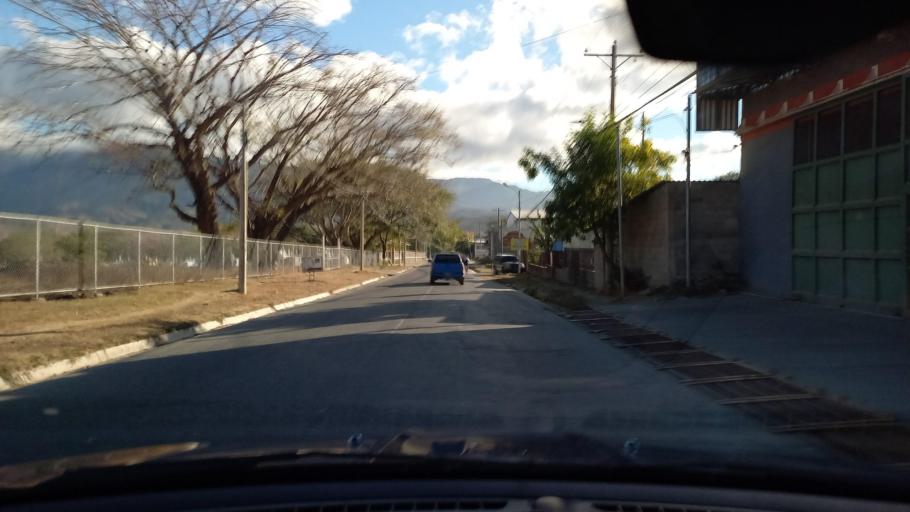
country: SV
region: Santa Ana
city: Metapan
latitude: 14.3272
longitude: -89.4565
